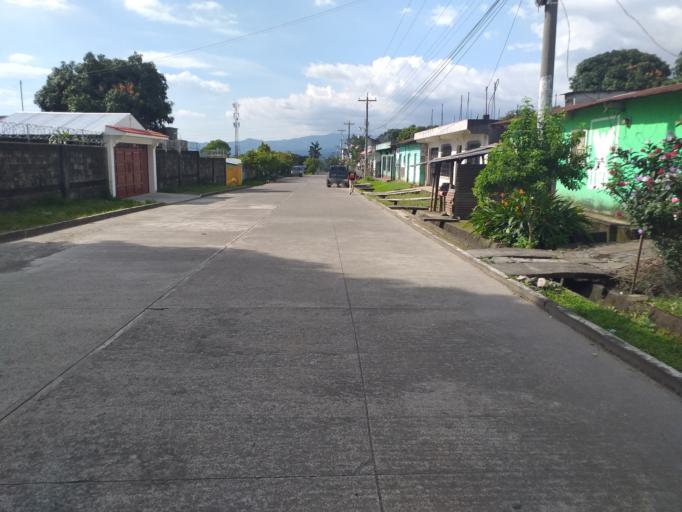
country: GT
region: Suchitepeque
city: Pueblo Nuevo
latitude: 14.6475
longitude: -91.5554
